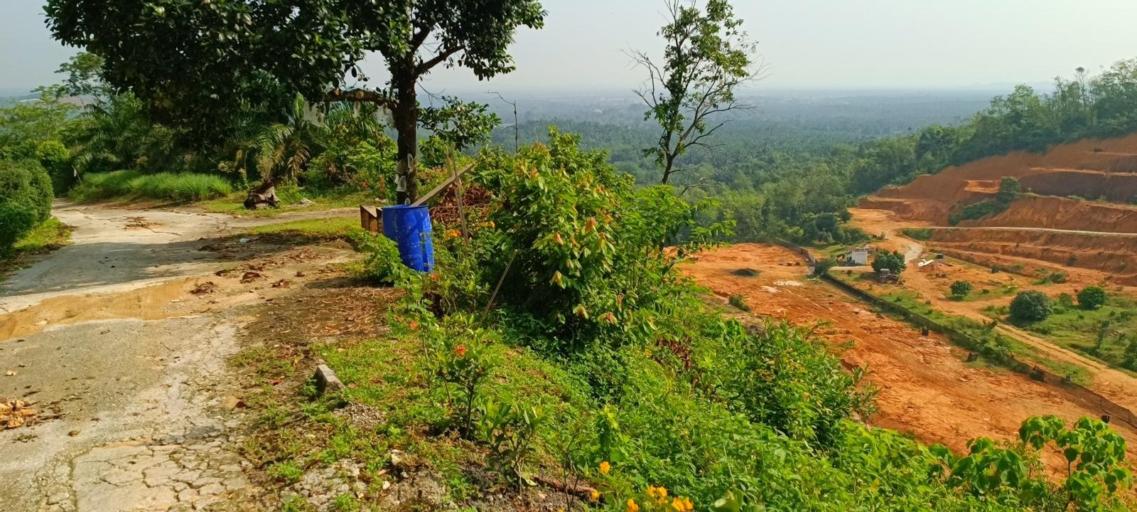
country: MY
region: Penang
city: Bukit Mertajam
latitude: 5.4093
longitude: 100.5083
